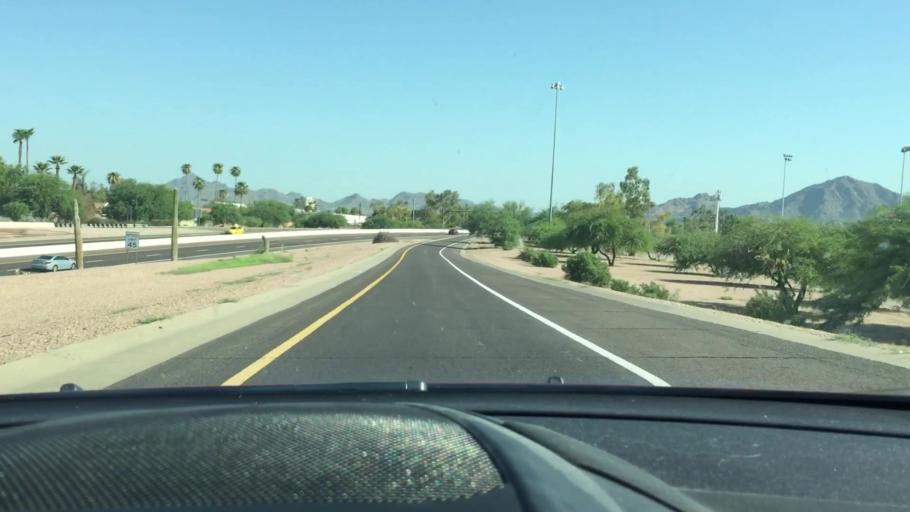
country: US
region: Arizona
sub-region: Maricopa County
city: Tempe Junction
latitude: 33.4605
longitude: -111.9816
